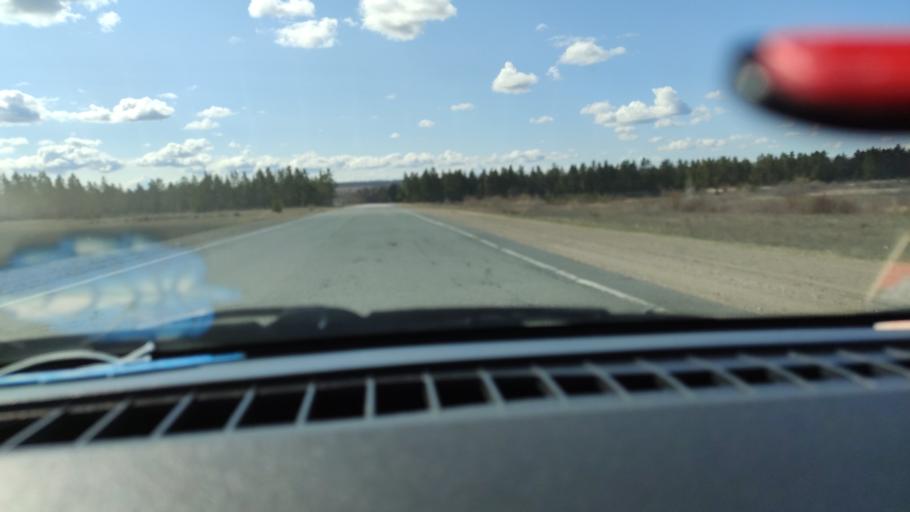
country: RU
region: Samara
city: Varlamovo
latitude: 53.1457
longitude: 48.2846
